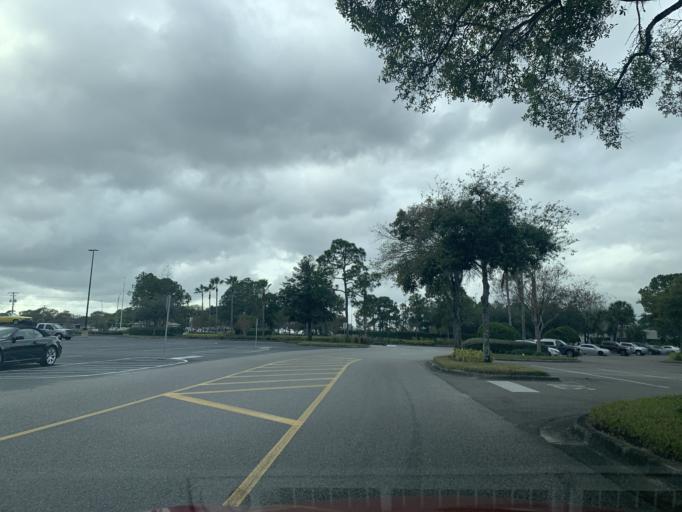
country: US
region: Florida
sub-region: Hillsborough County
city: East Lake-Orient Park
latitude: 27.9903
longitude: -82.3915
